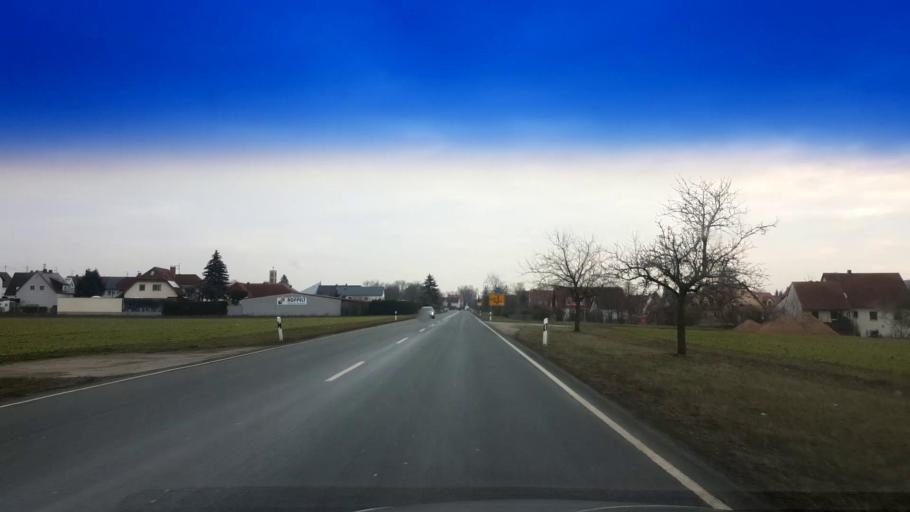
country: DE
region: Bavaria
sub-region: Upper Franconia
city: Altendorf
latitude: 49.8029
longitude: 11.0078
